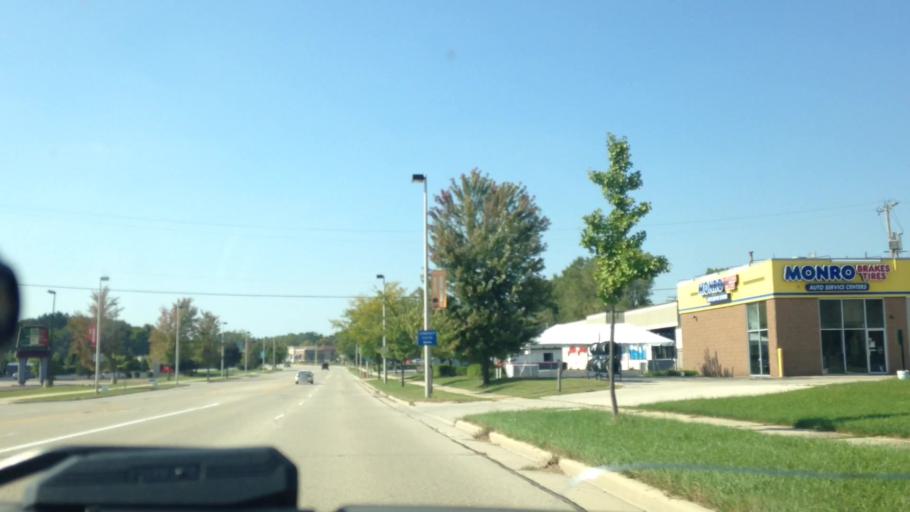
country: US
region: Wisconsin
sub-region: Waukesha County
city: Menomonee Falls
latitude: 43.1779
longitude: -88.0979
